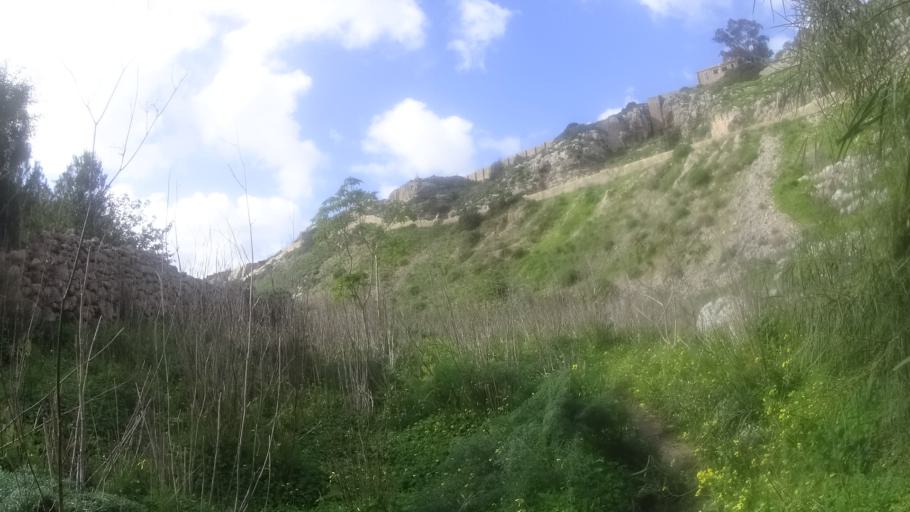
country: MT
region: Il-Mosta
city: Mosta
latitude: 35.9206
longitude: 14.4286
